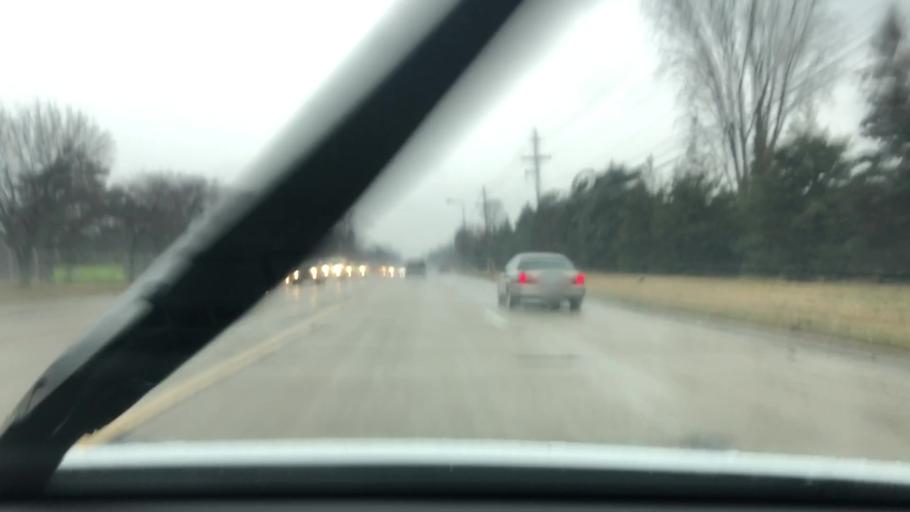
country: US
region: Michigan
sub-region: Oakland County
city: Troy
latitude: 42.5820
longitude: -83.1683
